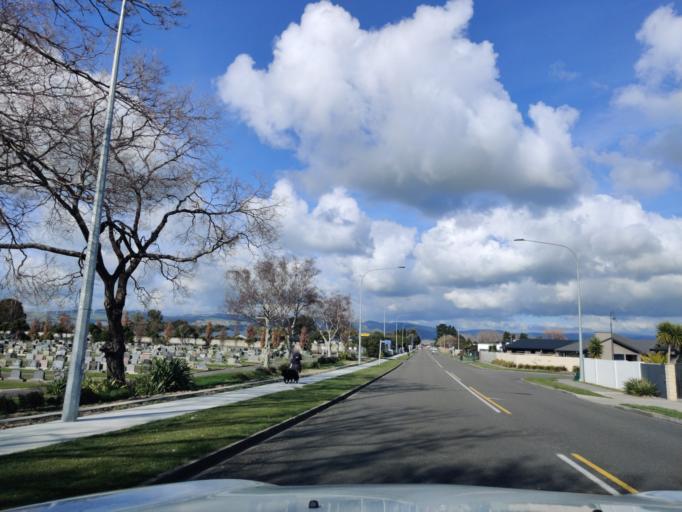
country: NZ
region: Manawatu-Wanganui
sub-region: Palmerston North City
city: Palmerston North
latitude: -40.3244
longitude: 175.6612
